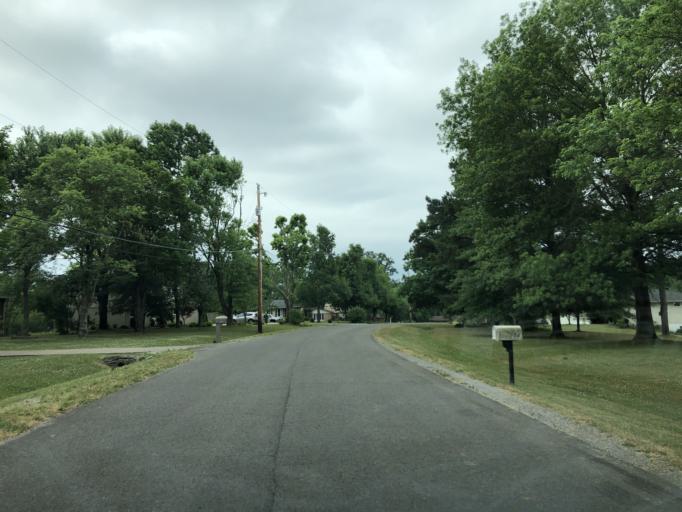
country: US
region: Tennessee
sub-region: Davidson County
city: Goodlettsville
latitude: 36.2916
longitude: -86.7292
